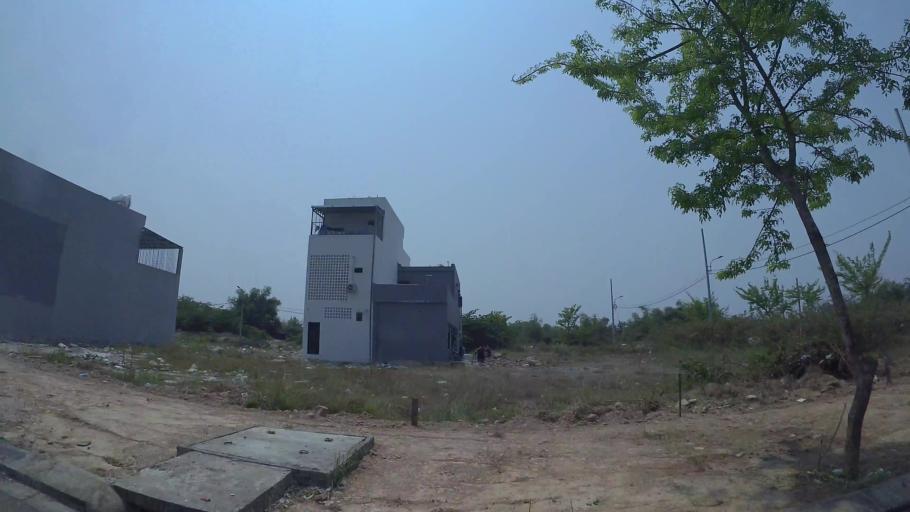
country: VN
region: Da Nang
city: Cam Le
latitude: 16.0191
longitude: 108.2265
